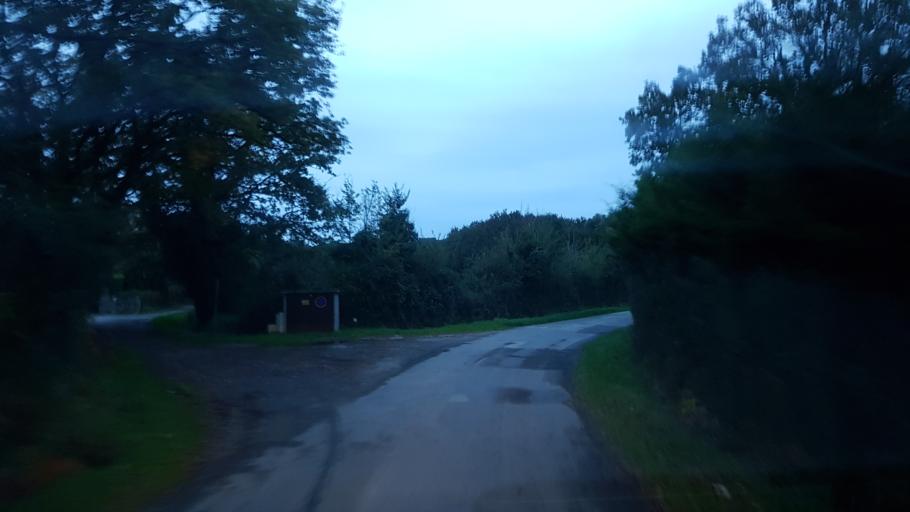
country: FR
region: Brittany
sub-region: Departement du Morbihan
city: Sarzeau
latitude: 47.5435
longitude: -2.8133
